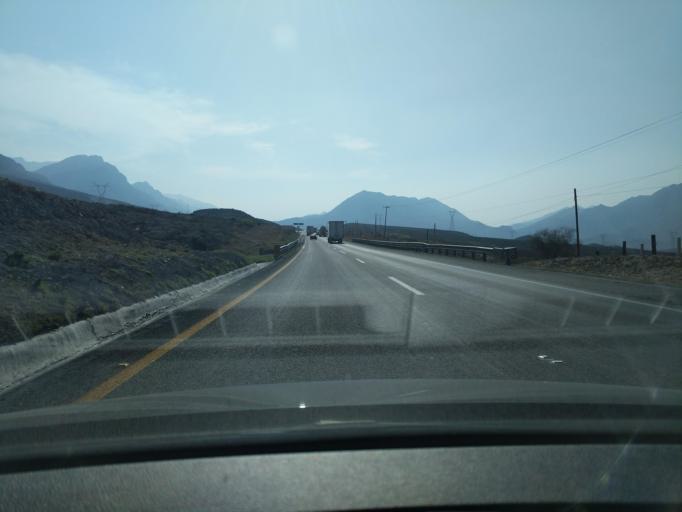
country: MX
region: Nuevo Leon
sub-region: Garcia
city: Las Torres de Guadalupe
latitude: 25.6786
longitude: -100.6696
